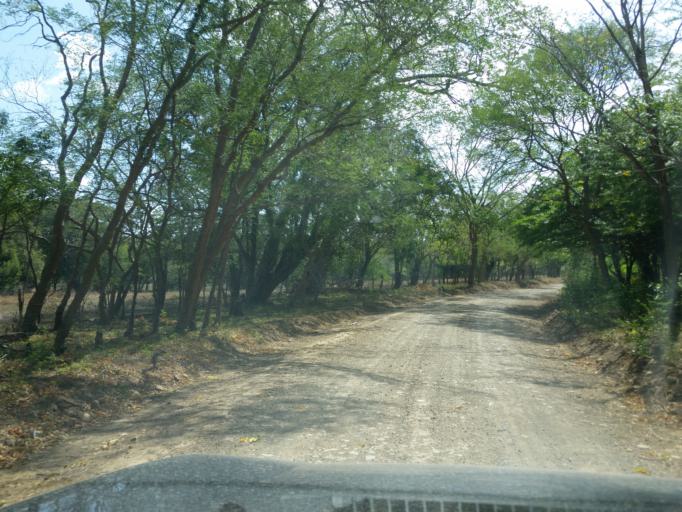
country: NI
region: Rivas
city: San Juan del Sur
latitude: 11.1364
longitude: -85.7815
